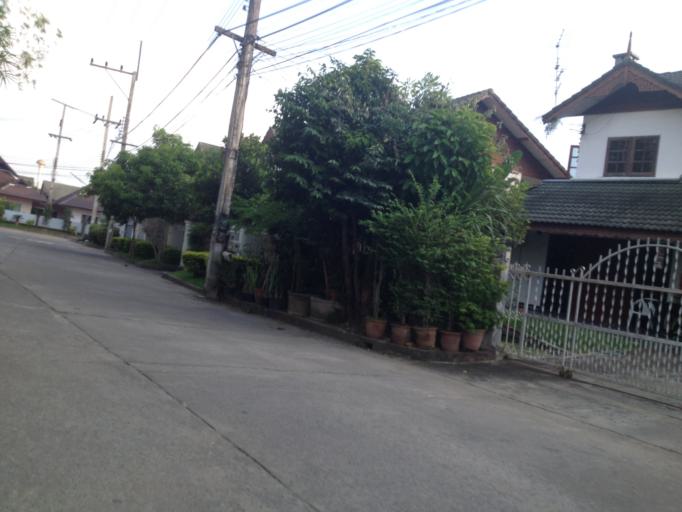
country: TH
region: Chiang Mai
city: Hang Dong
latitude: 18.7443
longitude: 98.9348
